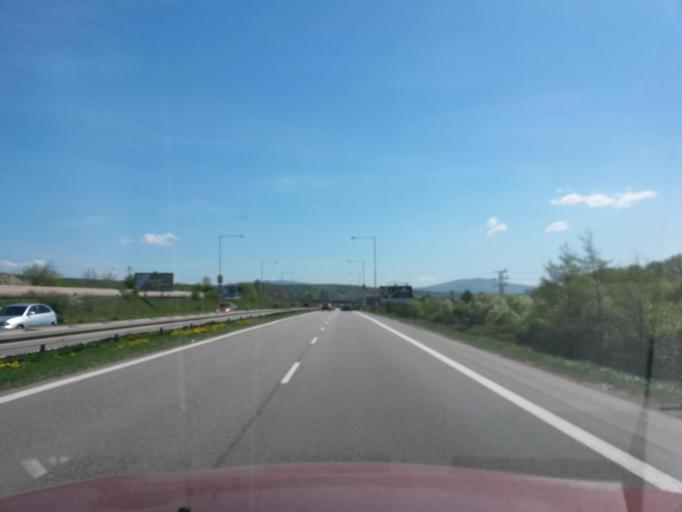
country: SK
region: Kosicky
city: Kosice
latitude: 48.6881
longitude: 21.2519
